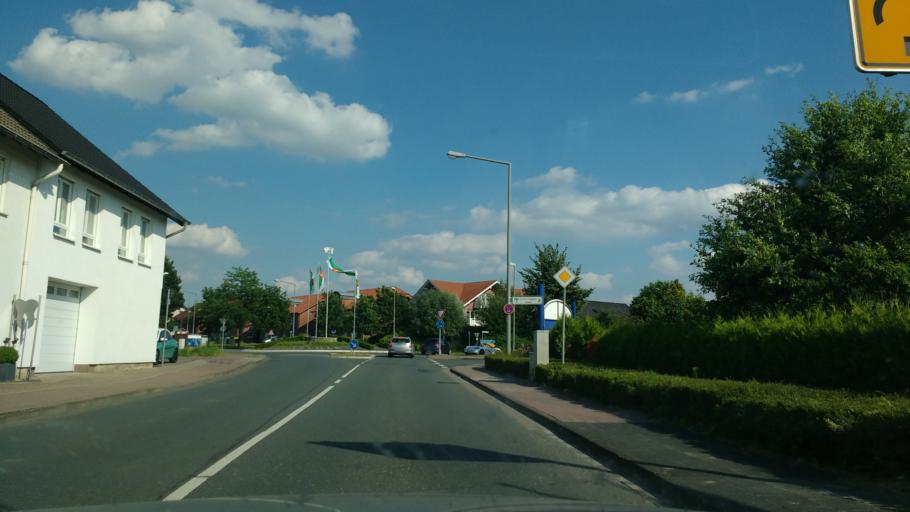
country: DE
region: North Rhine-Westphalia
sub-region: Regierungsbezirk Detmold
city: Salzkotten
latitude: 51.6709
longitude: 8.6147
